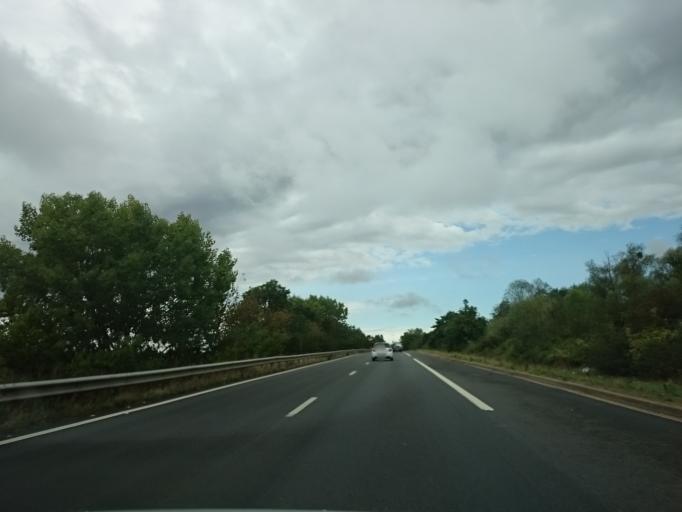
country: FR
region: Ile-de-France
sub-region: Departement de l'Essonne
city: Saclay
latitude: 48.7368
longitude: 2.1753
